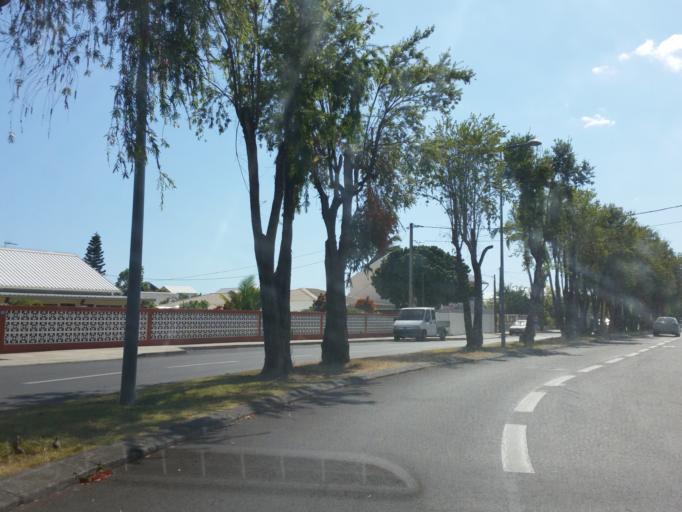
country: RE
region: Reunion
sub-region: Reunion
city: Saint-Paul
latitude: -20.9867
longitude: 55.2883
